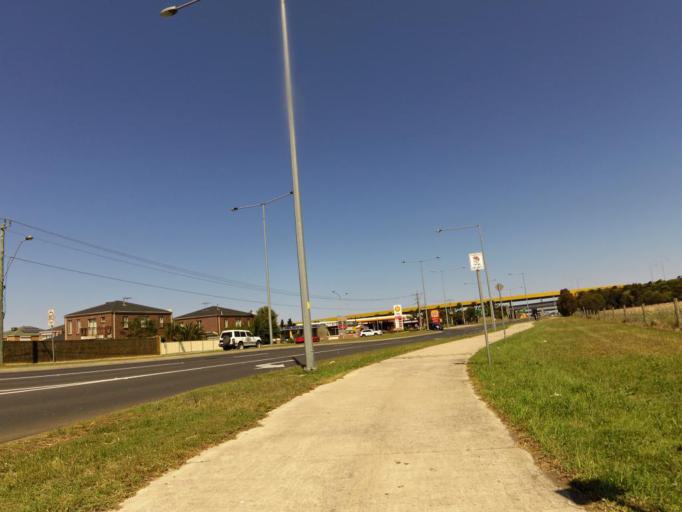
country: AU
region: Victoria
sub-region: Brimbank
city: Derrimut
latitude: -37.7948
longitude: 144.7895
